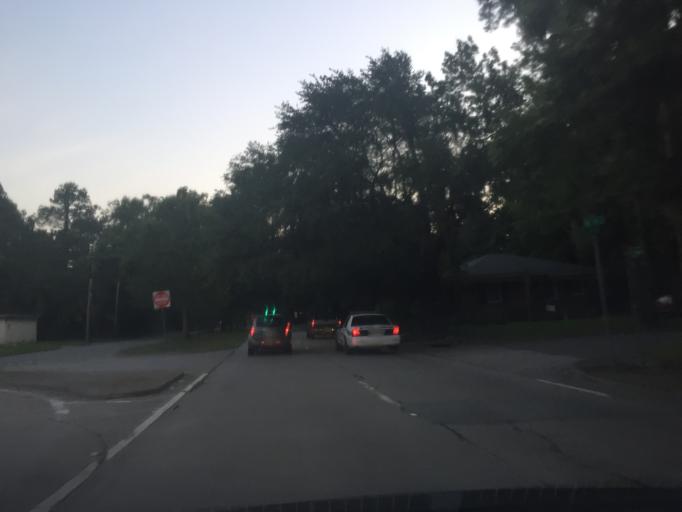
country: US
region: Georgia
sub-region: Chatham County
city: Savannah
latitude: 32.0331
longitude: -81.1064
